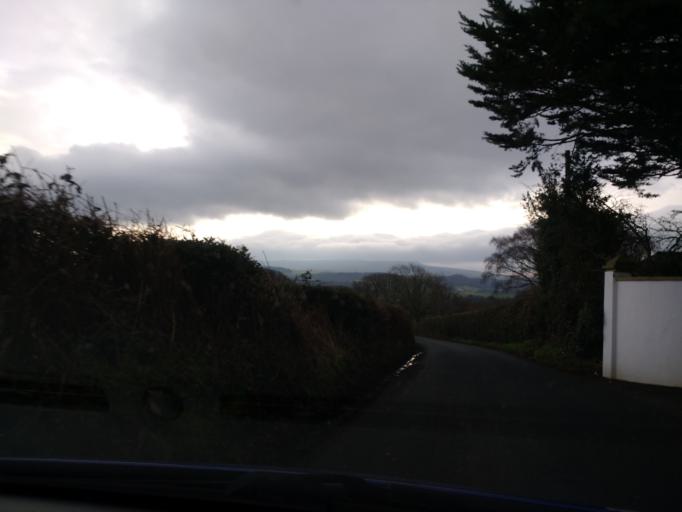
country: GB
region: England
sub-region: Lancashire
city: Caton
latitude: 54.0858
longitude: -2.7416
